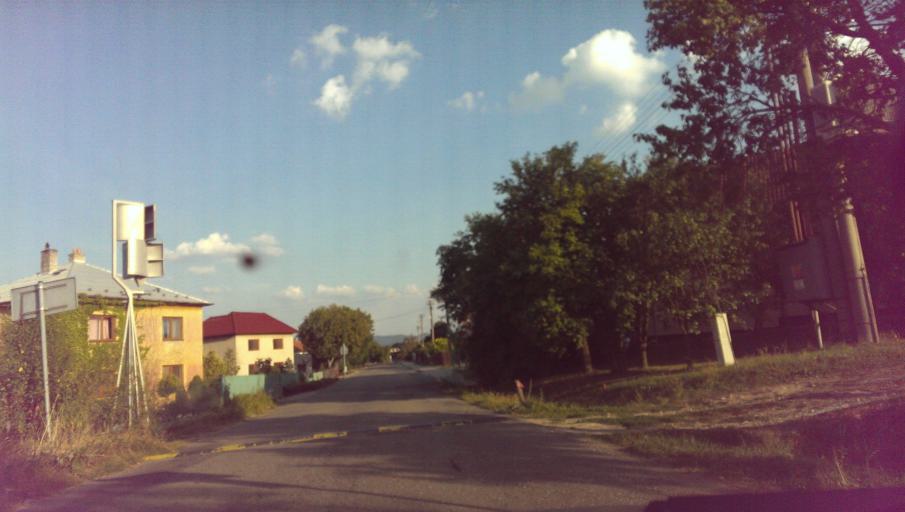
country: CZ
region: Zlin
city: Hvozdna
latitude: 49.2399
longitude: 17.7711
